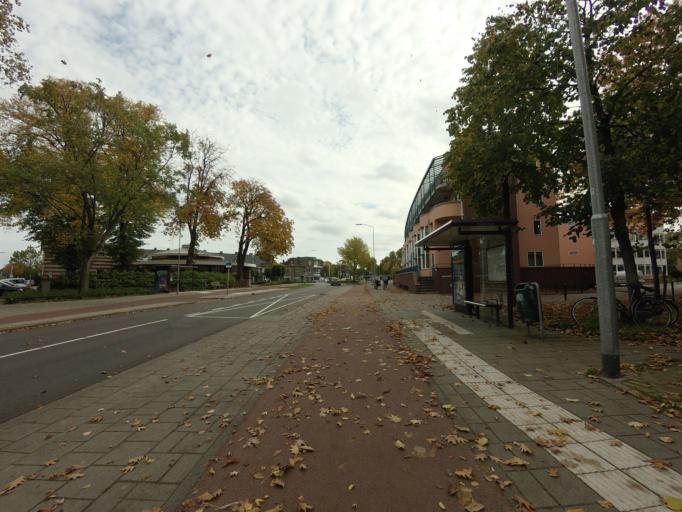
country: NL
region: North Brabant
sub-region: Gemeente Breda
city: Breda
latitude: 51.5787
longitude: 4.7899
